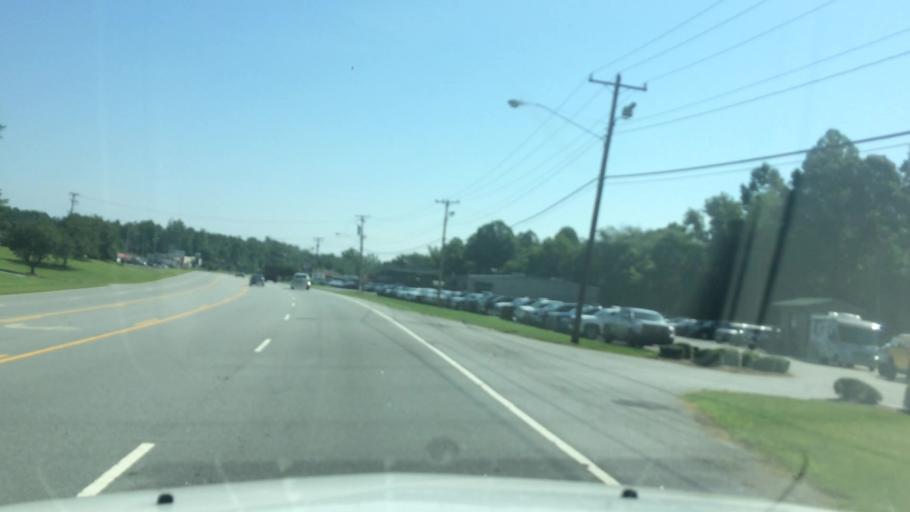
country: US
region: North Carolina
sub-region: Caldwell County
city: Lenoir
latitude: 35.9210
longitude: -81.5073
